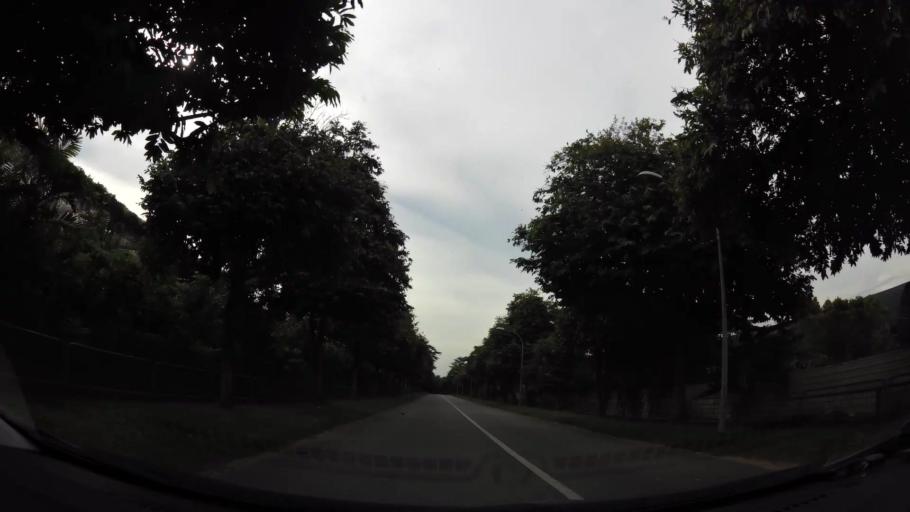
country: MY
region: Johor
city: Johor Bahru
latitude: 1.4356
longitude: 103.7109
